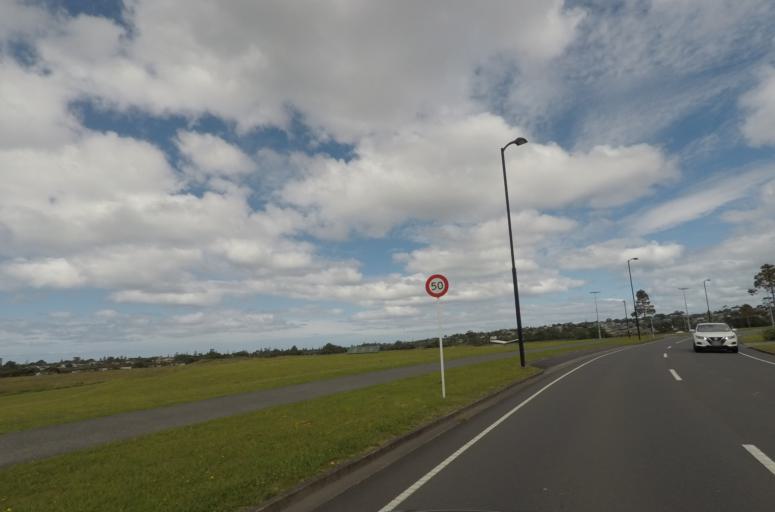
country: NZ
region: Auckland
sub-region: Auckland
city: Rothesay Bay
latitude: -36.5977
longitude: 174.6776
